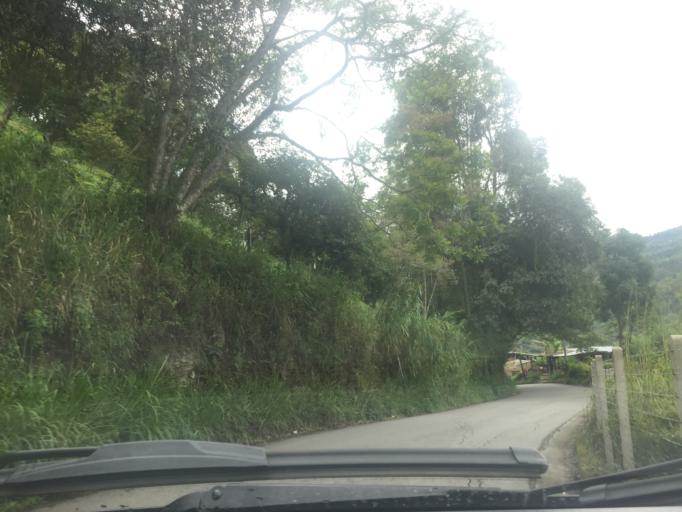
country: CO
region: Cundinamarca
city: San Francisco
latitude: 4.9828
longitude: -74.2911
